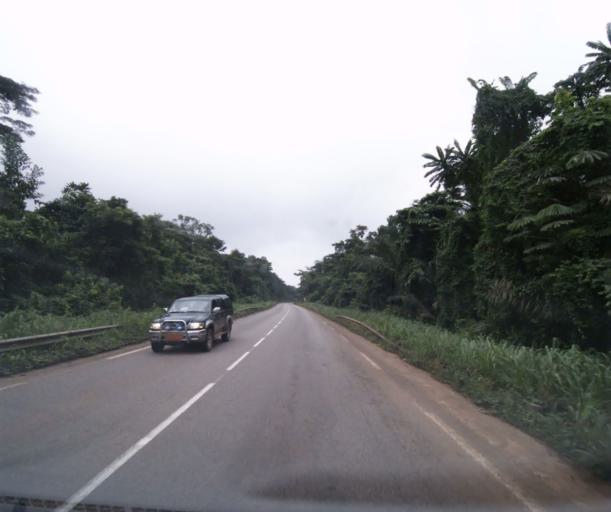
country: CM
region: Centre
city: Eseka
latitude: 3.8723
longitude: 10.6598
